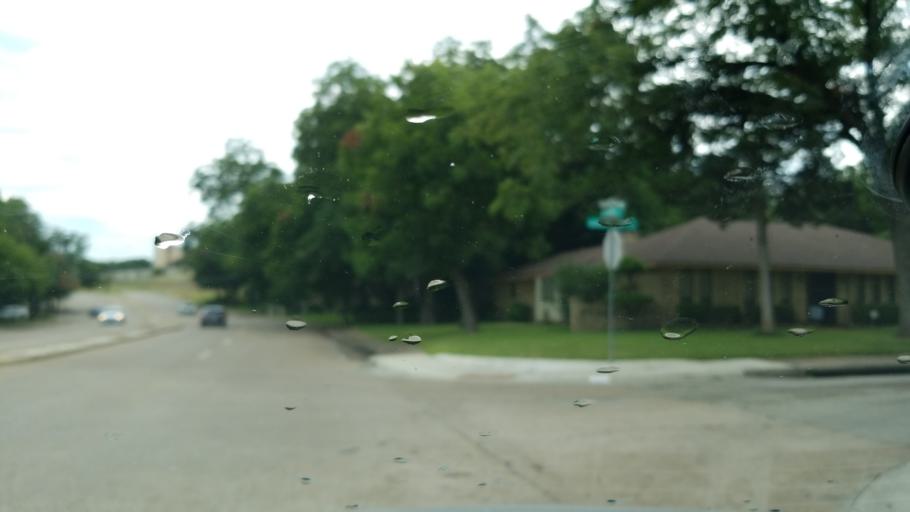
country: US
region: Texas
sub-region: Dallas County
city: Duncanville
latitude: 32.6727
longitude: -96.8372
